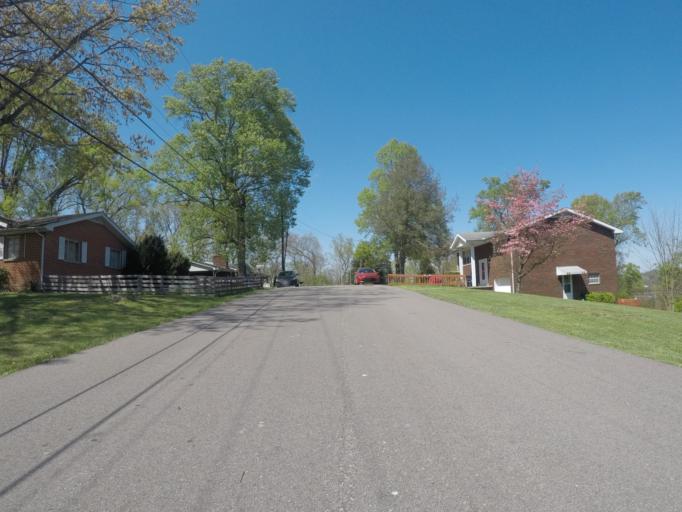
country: US
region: West Virginia
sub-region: Wayne County
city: Kenova
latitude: 38.3961
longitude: -82.5854
